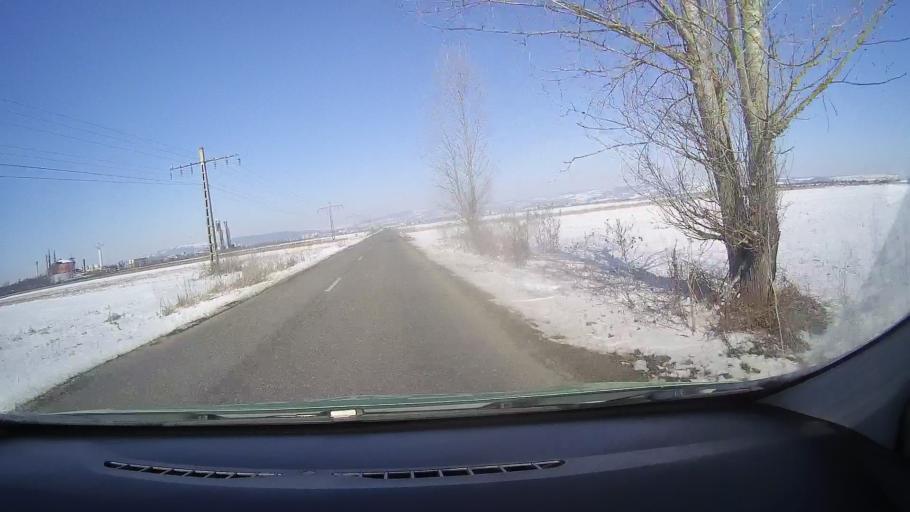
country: RO
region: Brasov
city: Fogarasch
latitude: 45.8039
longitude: 24.9919
